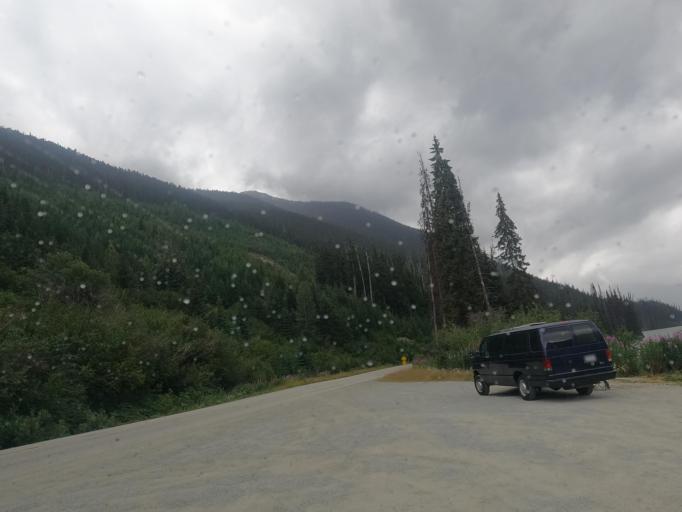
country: CA
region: British Columbia
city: Lillooet
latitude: 50.4002
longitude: -122.3132
